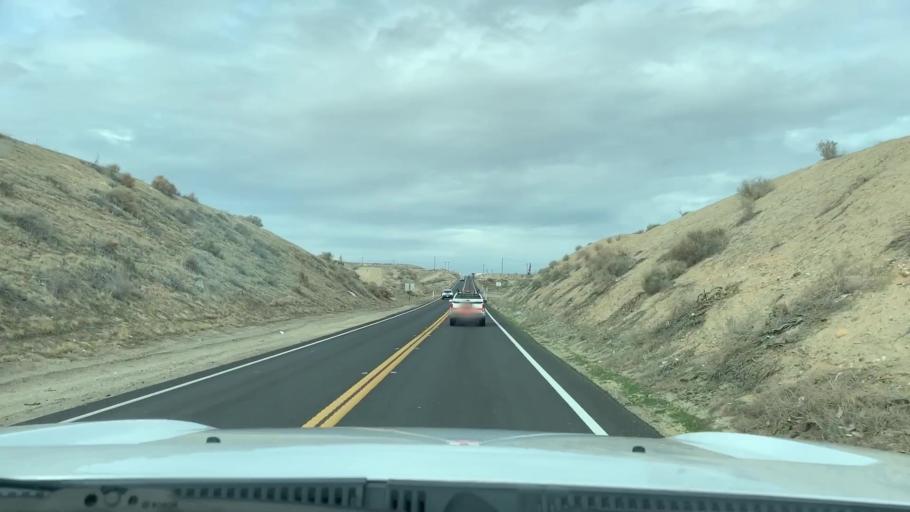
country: US
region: California
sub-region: Kern County
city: South Taft
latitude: 35.1104
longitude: -119.4249
